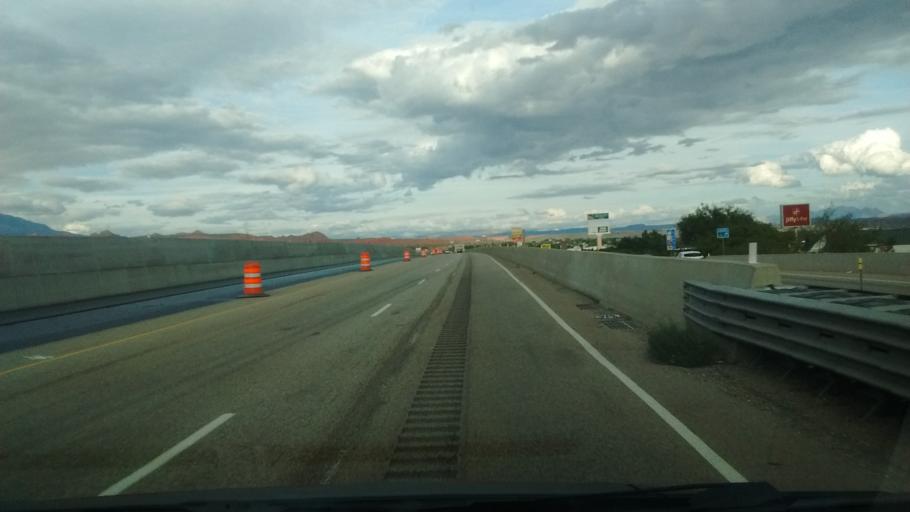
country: US
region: Utah
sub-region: Washington County
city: Washington
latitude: 37.1268
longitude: -113.5281
